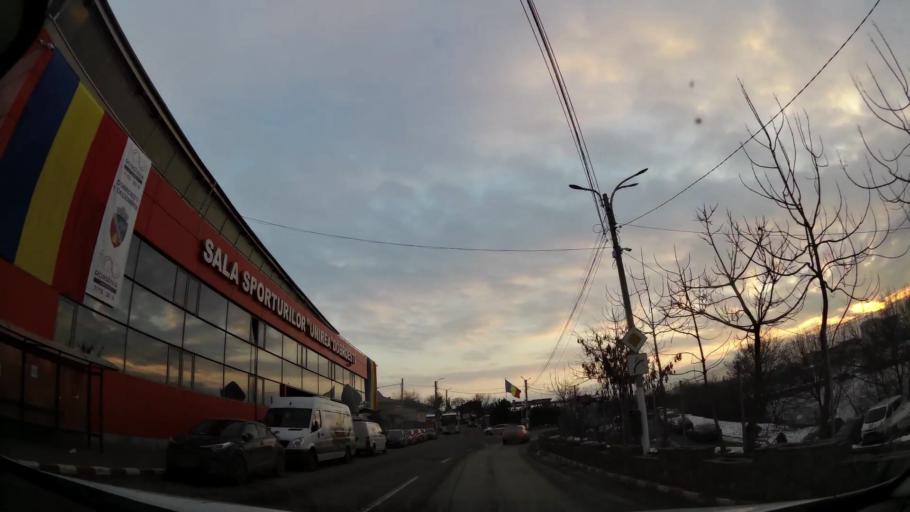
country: RO
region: Ilfov
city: Dobroesti
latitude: 44.4520
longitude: 26.1791
